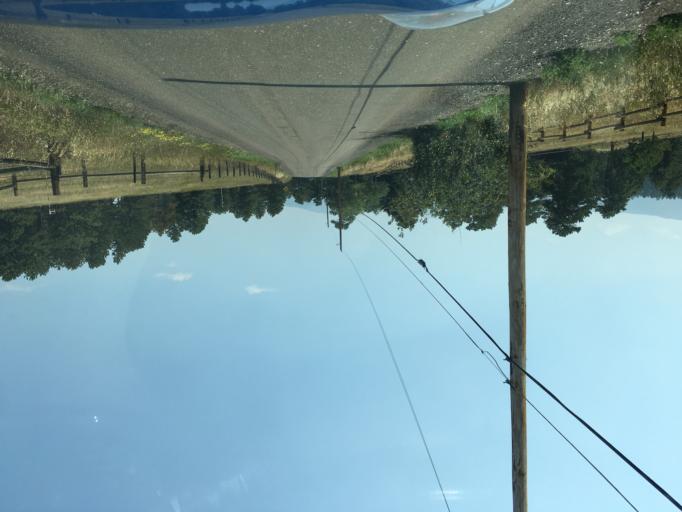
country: US
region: Colorado
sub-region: Jefferson County
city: Genesee
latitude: 39.7171
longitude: -105.2969
